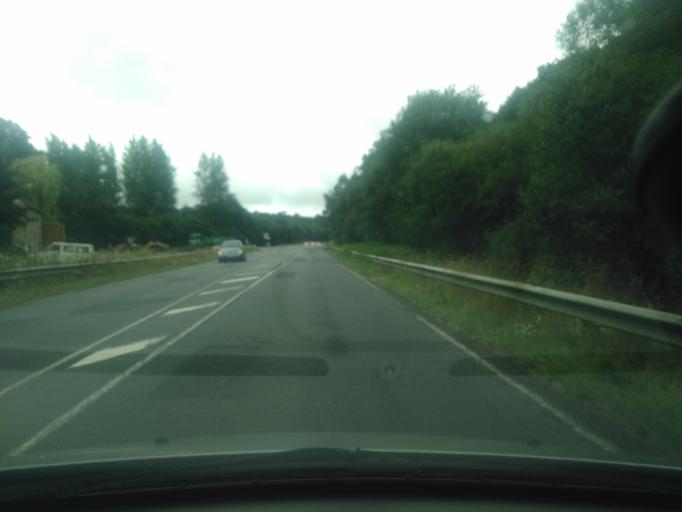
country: FR
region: Brittany
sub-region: Departement des Cotes-d'Armor
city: Quintin
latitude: 48.3615
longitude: -2.9553
